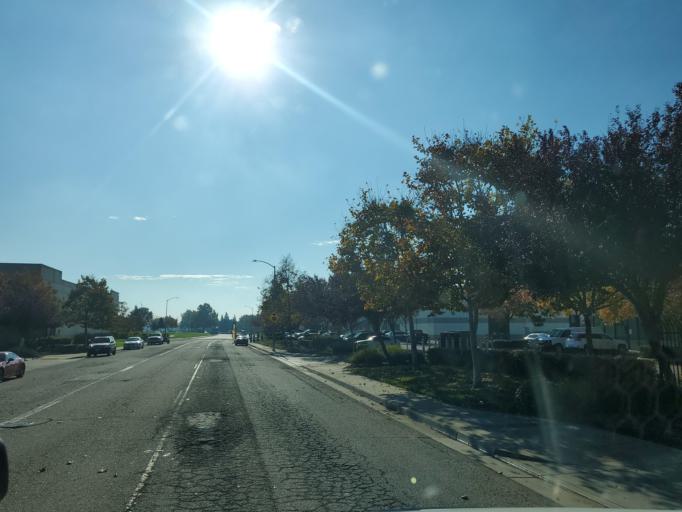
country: US
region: California
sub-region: San Joaquin County
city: Kennedy
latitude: 37.9132
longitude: -121.2475
